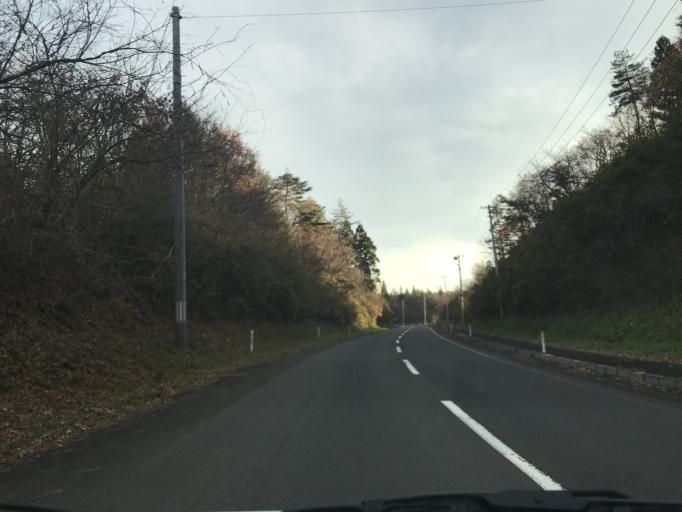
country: JP
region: Iwate
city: Ichinoseki
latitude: 38.9866
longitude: 141.0678
